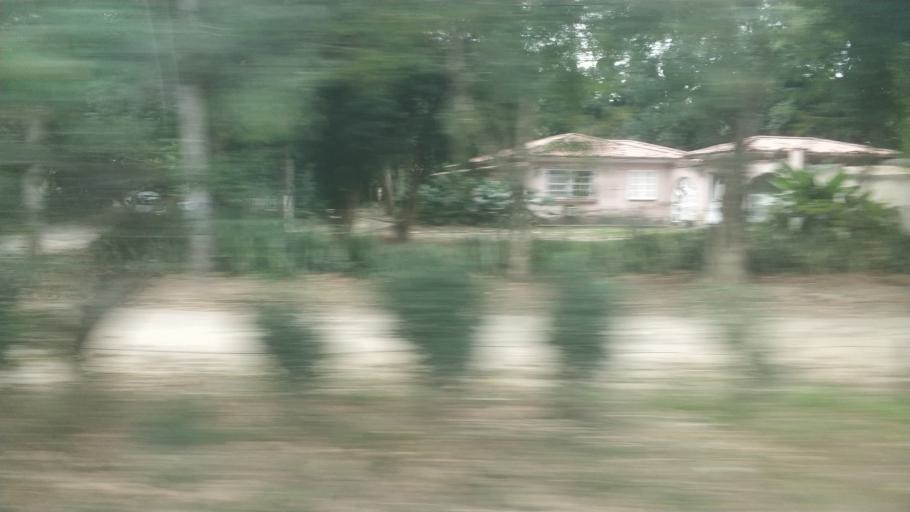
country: BR
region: Rio de Janeiro
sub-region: Seropedica
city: Seropedica
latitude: -22.7659
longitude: -43.6808
